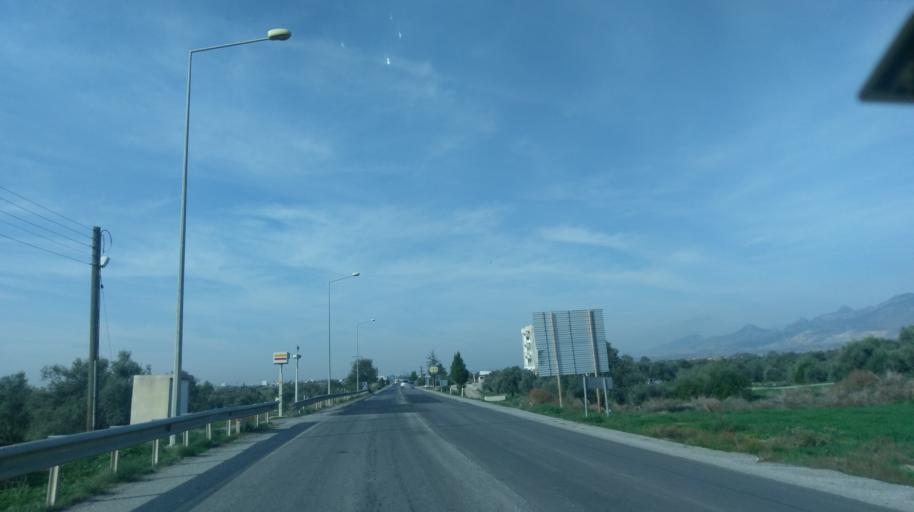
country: CY
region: Lefkosia
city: Geri
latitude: 35.2217
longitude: 33.5137
